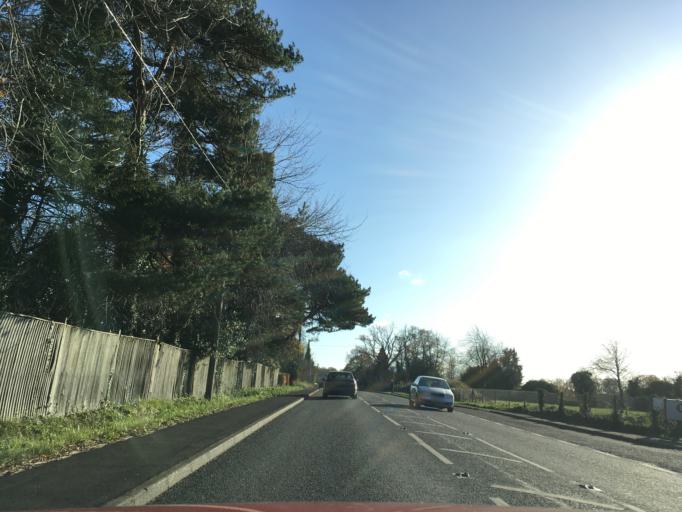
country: GB
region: England
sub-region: Hampshire
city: Colden Common
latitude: 50.9974
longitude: -1.3138
